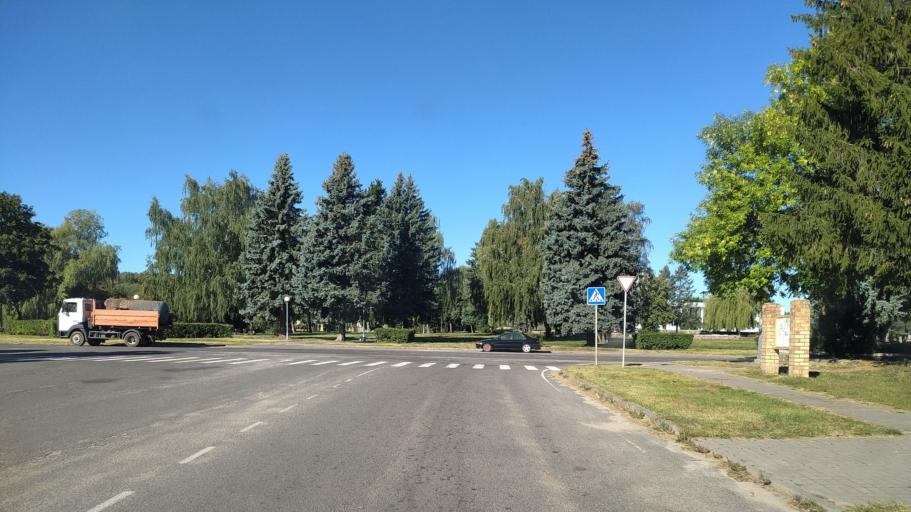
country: BY
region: Brest
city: Pruzhany
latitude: 52.4878
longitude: 24.7082
